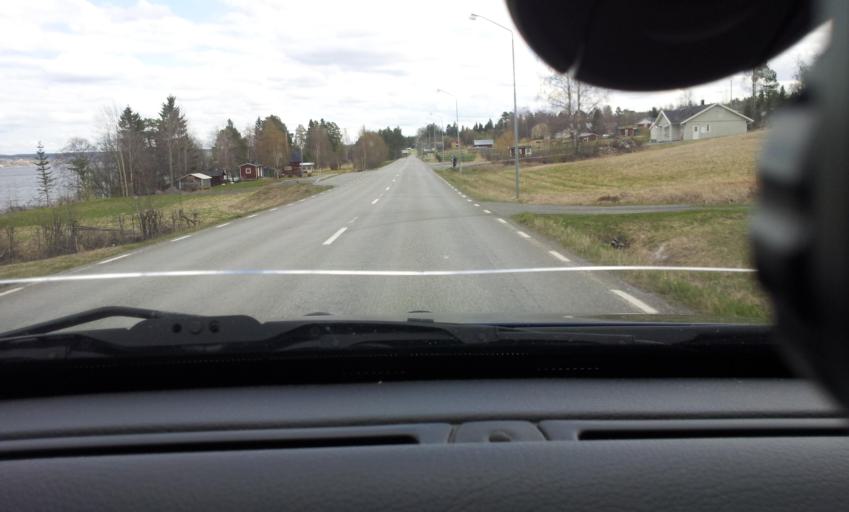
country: SE
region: Jaemtland
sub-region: OEstersunds Kommun
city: Ostersund
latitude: 63.1359
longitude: 14.6392
